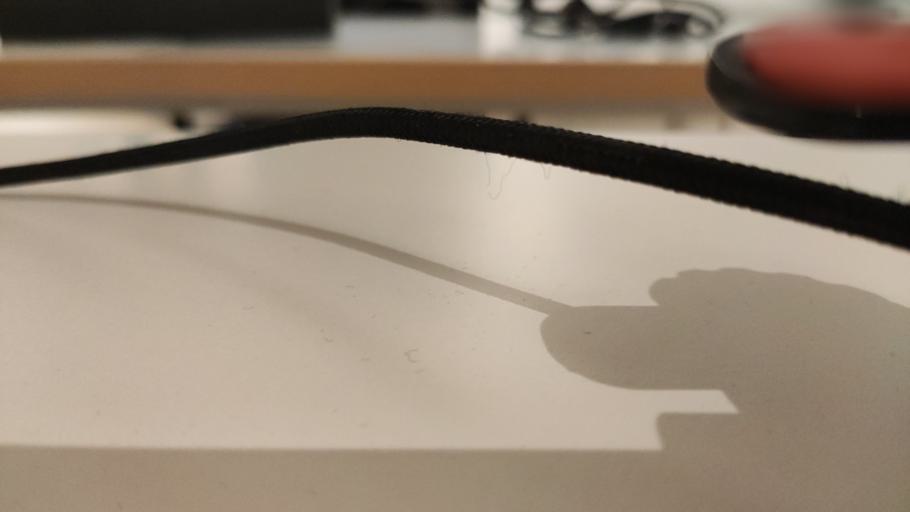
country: RU
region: Moskovskaya
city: Dorokhovo
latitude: 55.4009
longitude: 36.3814
